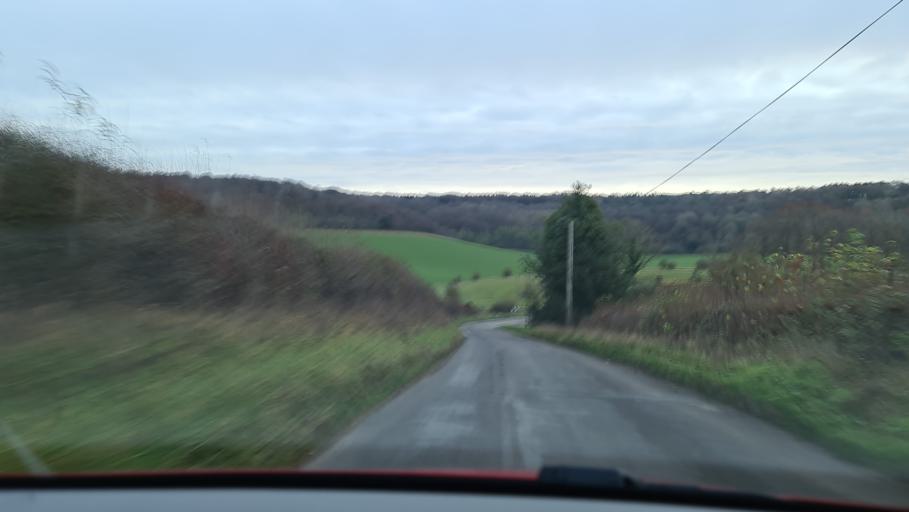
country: GB
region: England
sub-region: Buckinghamshire
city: Princes Risborough
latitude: 51.7162
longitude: -0.8155
